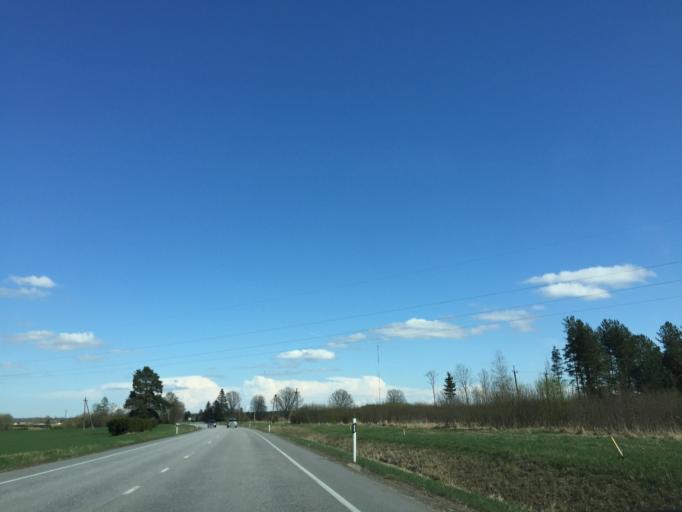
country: EE
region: Valgamaa
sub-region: Valga linn
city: Valga
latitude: 57.8623
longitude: 26.2049
